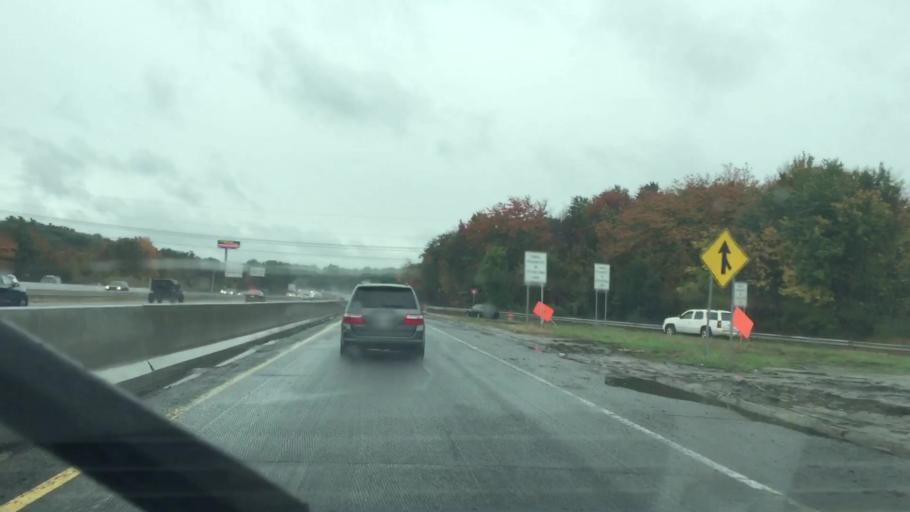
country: US
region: Massachusetts
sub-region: Essex County
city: Methuen
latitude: 42.7264
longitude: -71.2064
